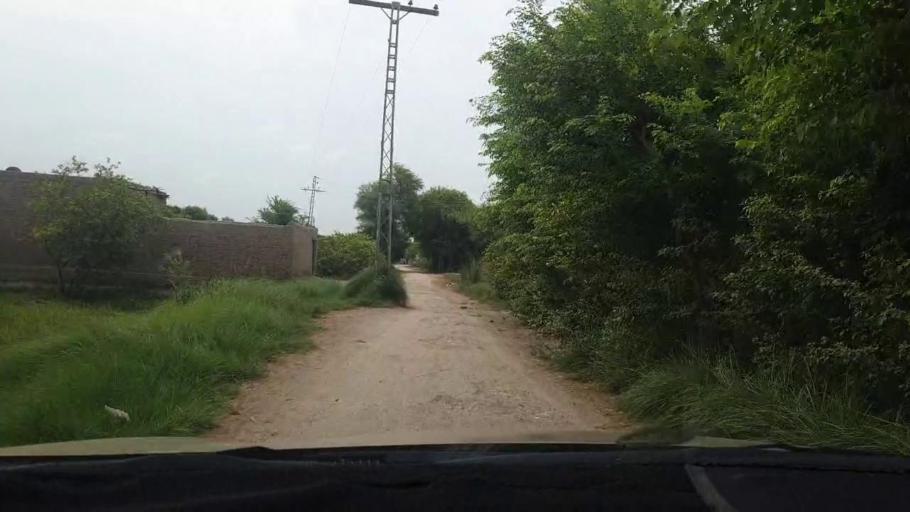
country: PK
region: Sindh
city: Naudero
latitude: 27.6318
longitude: 68.3094
